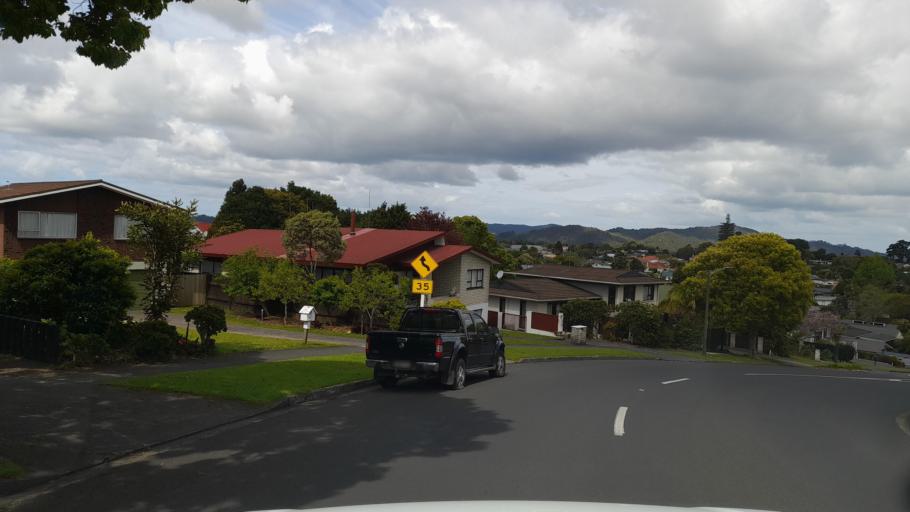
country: NZ
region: Northland
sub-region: Whangarei
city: Whangarei
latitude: -35.6862
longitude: 174.2992
